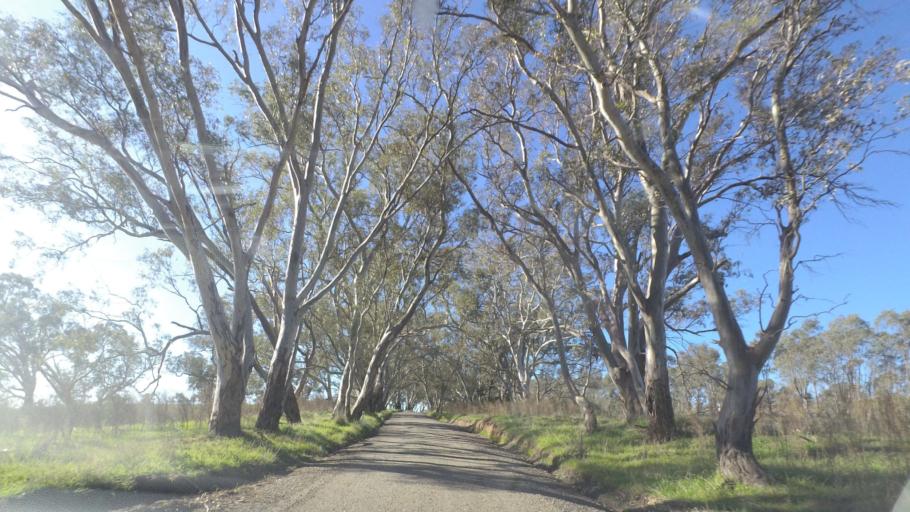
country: AU
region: Victoria
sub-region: Mount Alexander
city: Castlemaine
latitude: -36.9628
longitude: 144.3298
